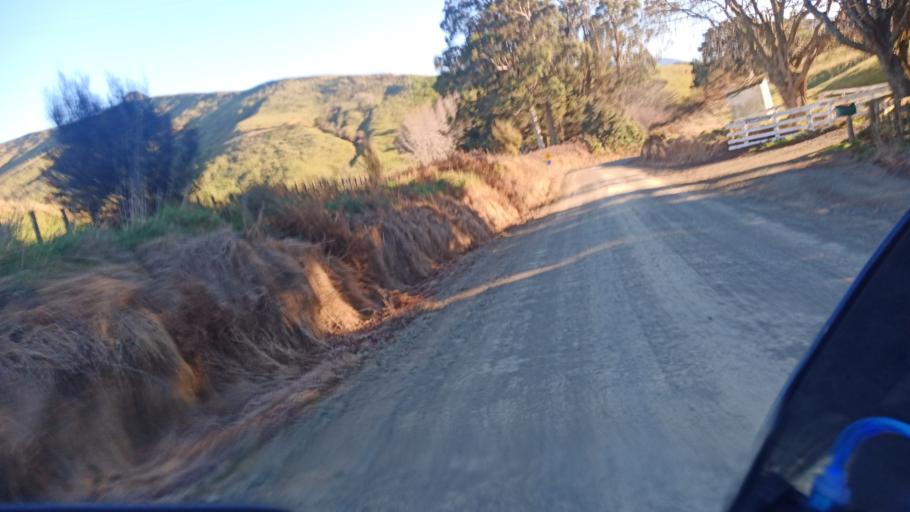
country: NZ
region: Bay of Plenty
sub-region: Opotiki District
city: Opotiki
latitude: -38.4601
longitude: 177.4252
